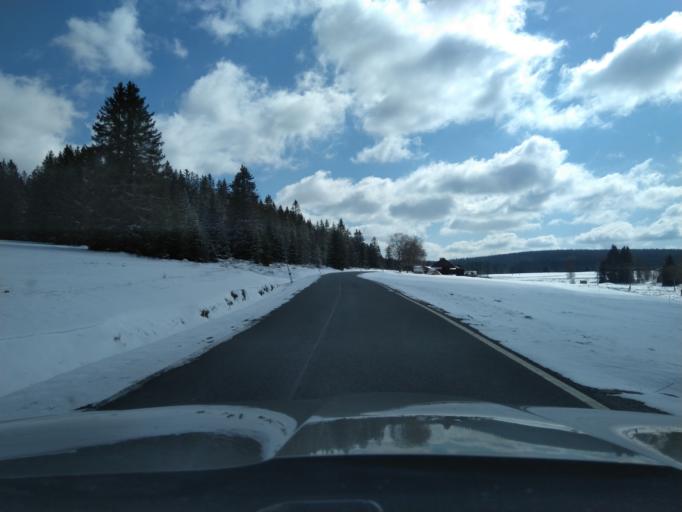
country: CZ
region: Plzensky
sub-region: Okres Klatovy
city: Kasperske Hory
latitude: 49.0509
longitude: 13.5728
